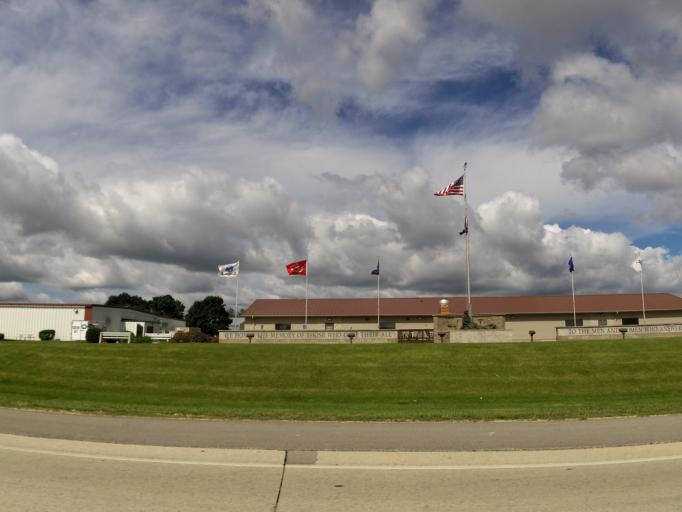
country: US
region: Minnesota
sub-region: Olmsted County
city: Stewartville
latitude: 43.8641
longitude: -92.4886
